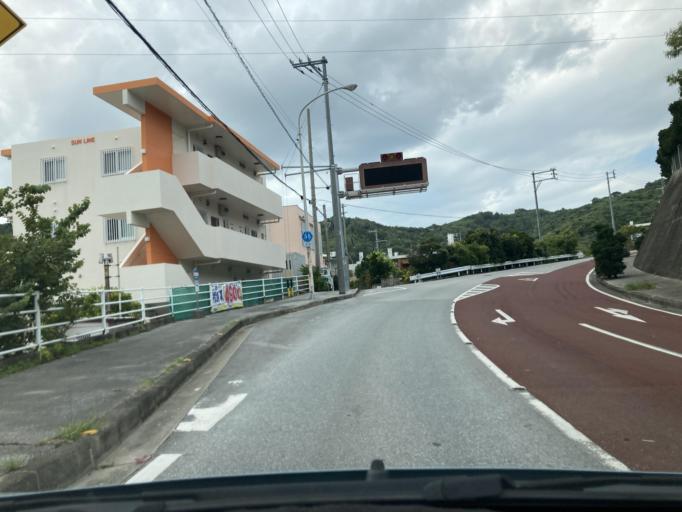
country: JP
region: Okinawa
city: Ginowan
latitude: 26.2554
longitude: 127.7845
